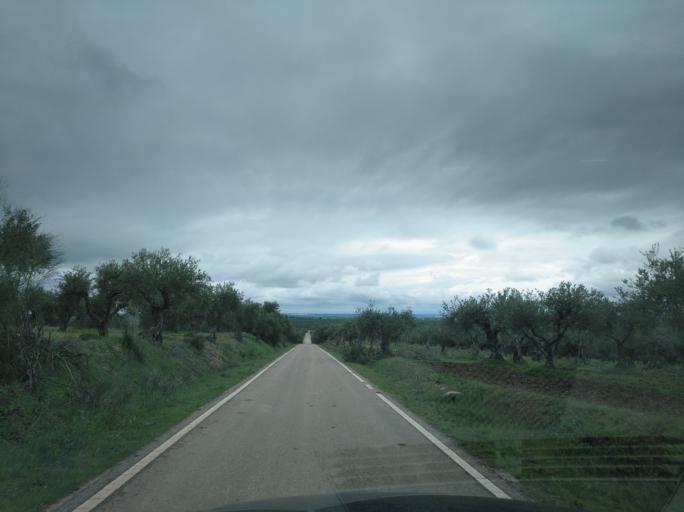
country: PT
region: Portalegre
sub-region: Campo Maior
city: Campo Maior
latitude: 38.9866
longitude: -7.0404
